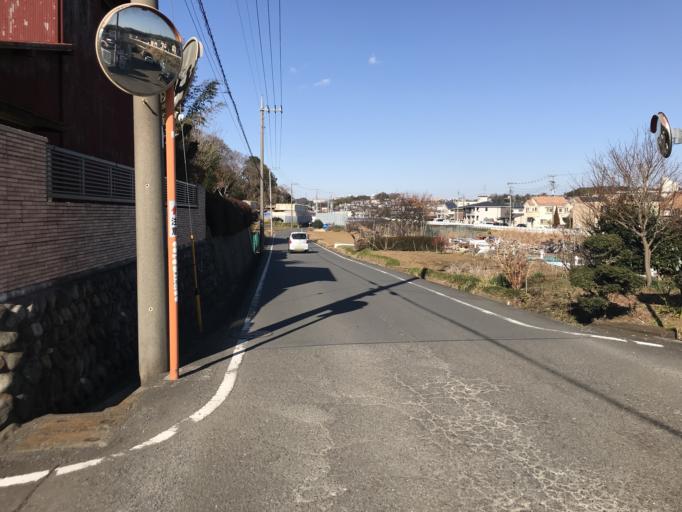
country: JP
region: Tokyo
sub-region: Machida-shi
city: Machida
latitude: 35.5721
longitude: 139.5088
